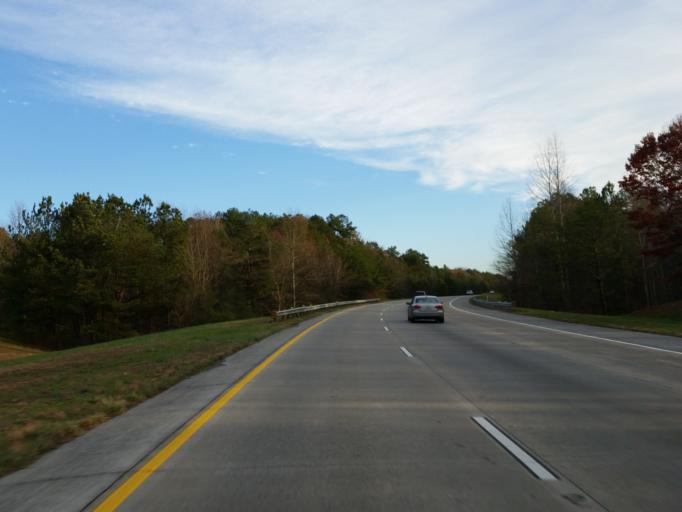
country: US
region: Georgia
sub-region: Cherokee County
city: Canton
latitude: 34.2699
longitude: -84.4660
